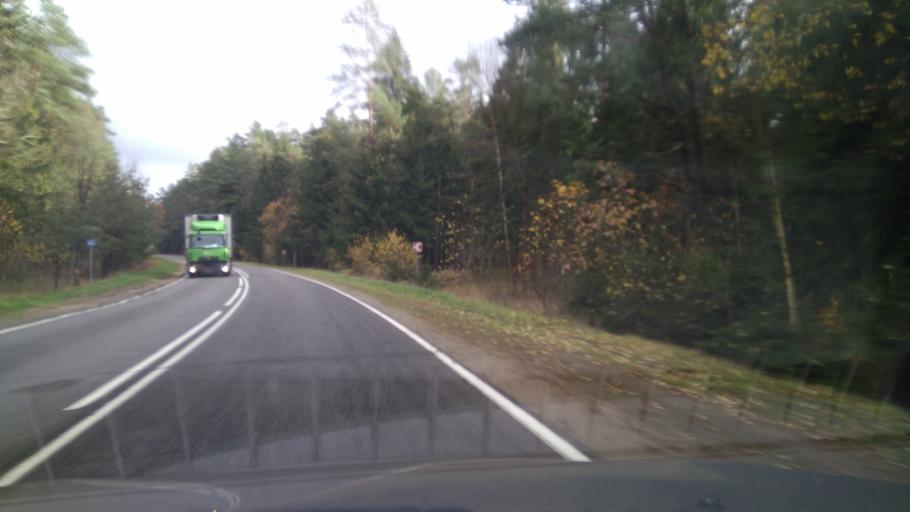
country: BY
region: Minsk
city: Slutsk
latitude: 53.2187
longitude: 27.5764
